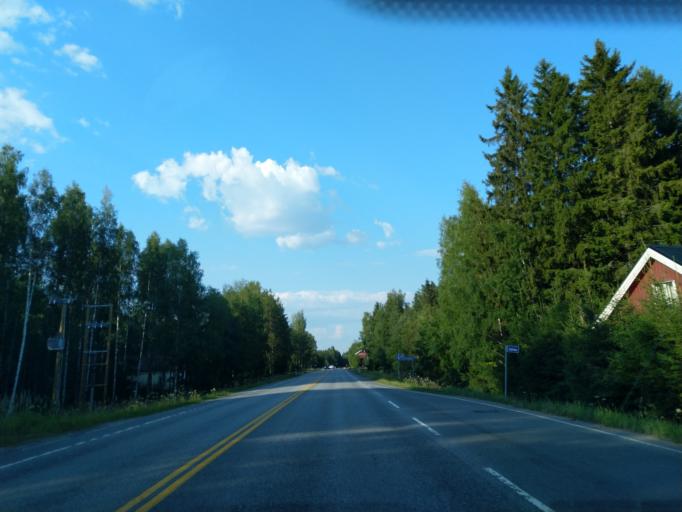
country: FI
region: Satakunta
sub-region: Pori
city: Laengelmaeki
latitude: 61.7421
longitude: 22.0928
